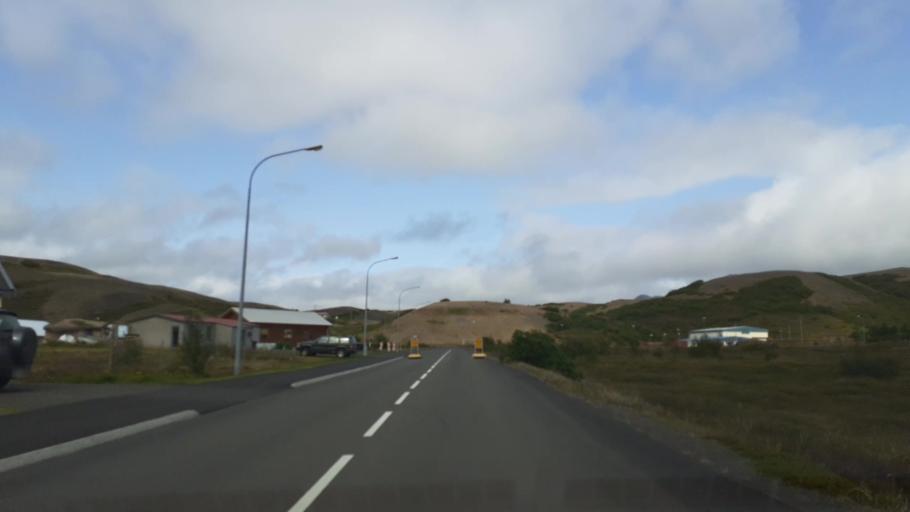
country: IS
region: Northeast
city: Laugar
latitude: 65.6405
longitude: -16.8957
